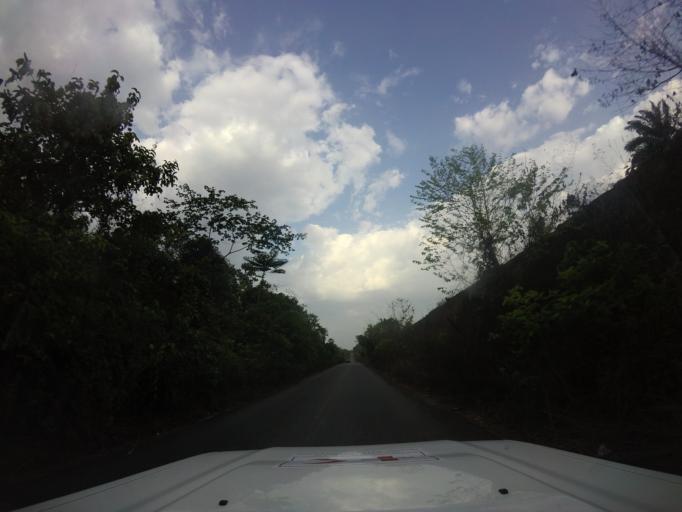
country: LR
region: Bomi
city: Tubmanburg
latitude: 6.6943
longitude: -10.8980
